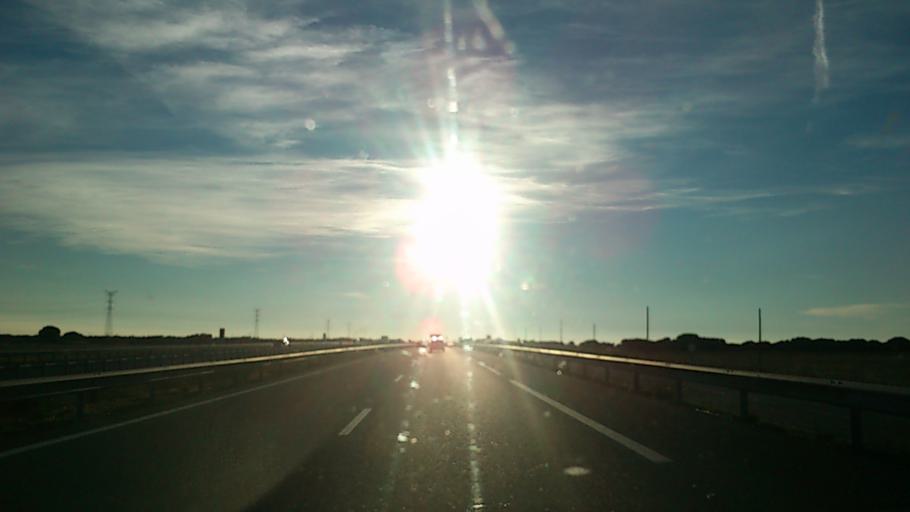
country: ES
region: Castille-La Mancha
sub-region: Provincia de Guadalajara
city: Gajanejos
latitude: 40.8363
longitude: -2.9010
